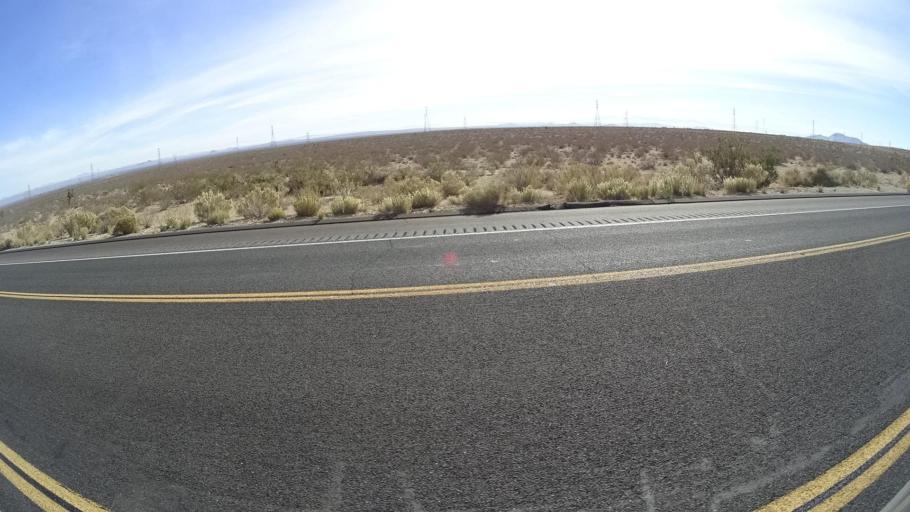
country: US
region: California
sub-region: Kern County
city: Mojave
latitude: 35.1228
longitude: -118.1745
